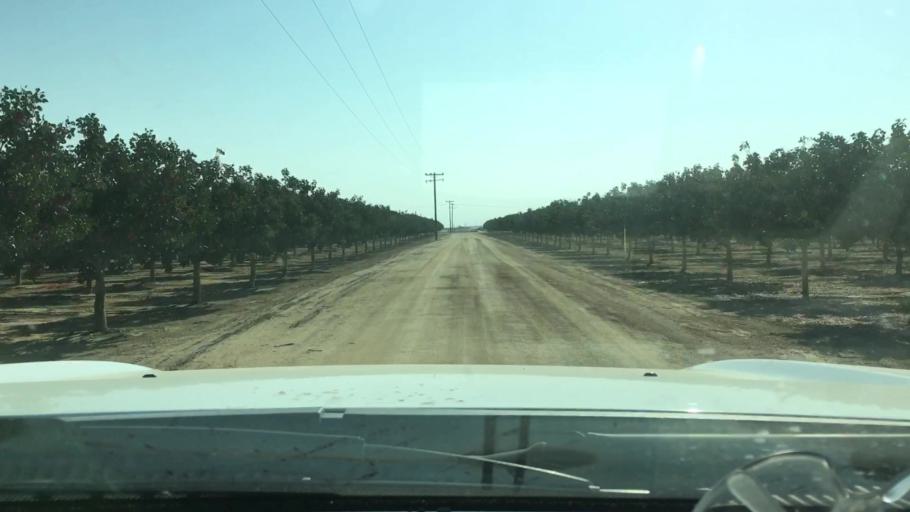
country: US
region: California
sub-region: Kern County
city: Lost Hills
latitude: 35.6302
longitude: -119.5832
